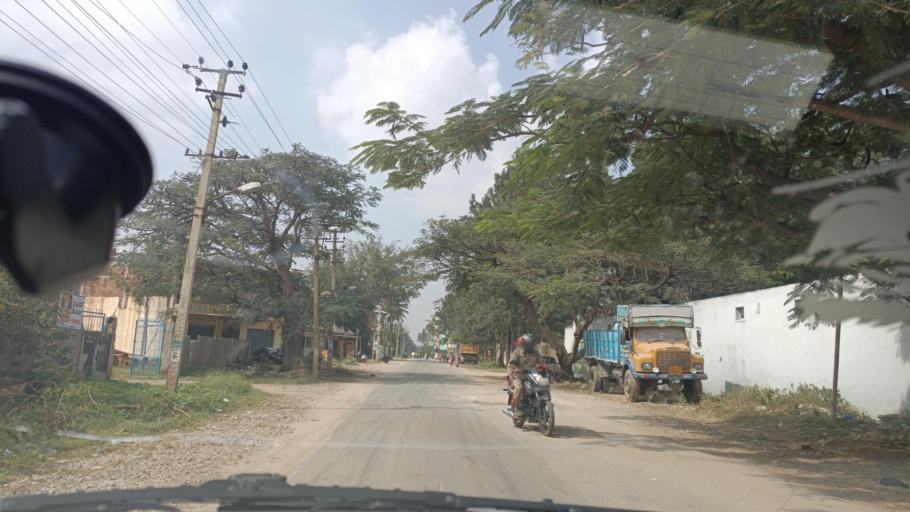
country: IN
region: Karnataka
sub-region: Bangalore Urban
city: Yelahanka
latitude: 13.1568
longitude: 77.6222
